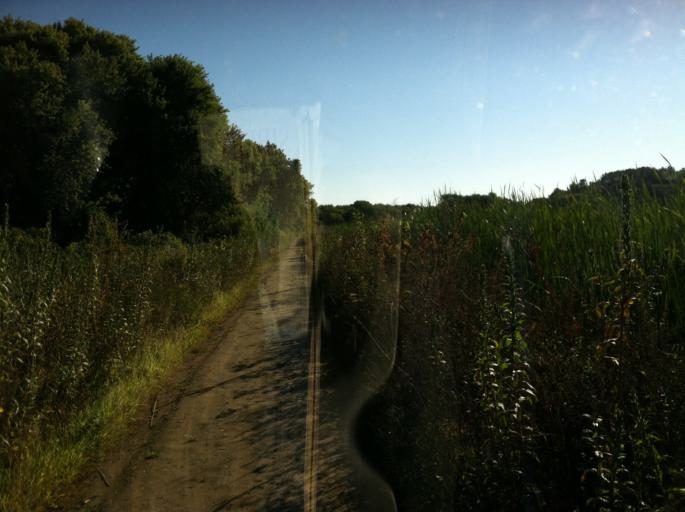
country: US
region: Massachusetts
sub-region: Middlesex County
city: Concord
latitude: 42.4810
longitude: -71.3292
